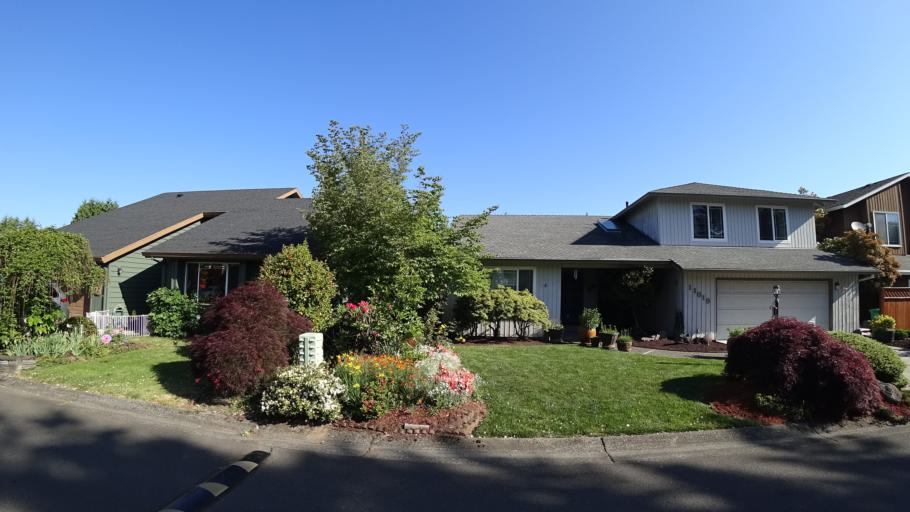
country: US
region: Oregon
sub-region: Multnomah County
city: Lents
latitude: 45.4700
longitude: -122.5436
